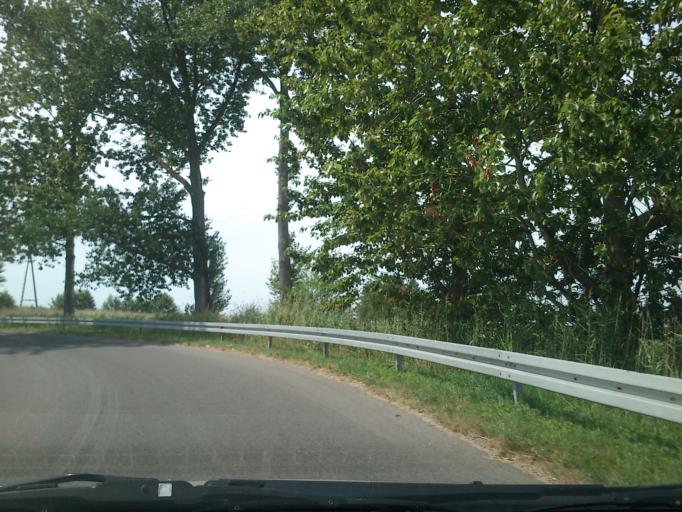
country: PL
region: West Pomeranian Voivodeship
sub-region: Powiat kamienski
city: Miedzyzdroje
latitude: 53.8900
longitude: 14.4348
